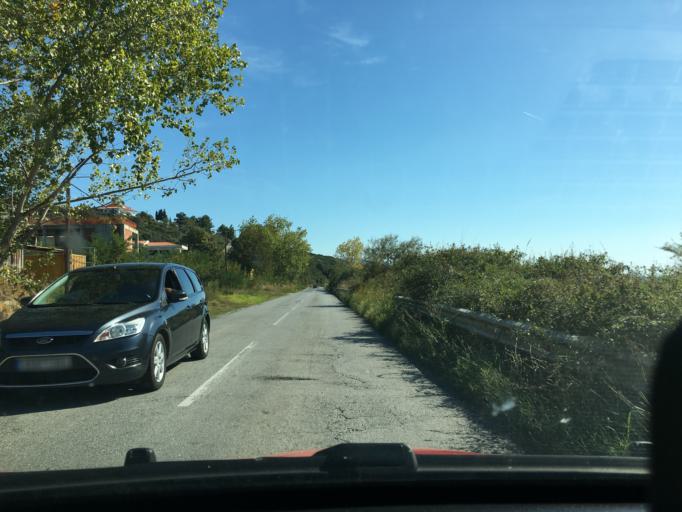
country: GR
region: Central Macedonia
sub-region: Nomos Chalkidikis
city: Nea Roda
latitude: 40.3613
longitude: 23.9308
